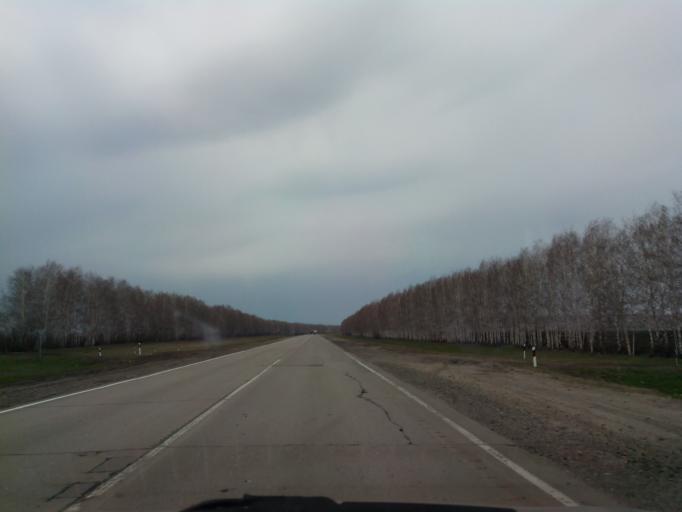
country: RU
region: Tambov
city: Znamenka
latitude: 52.2708
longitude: 41.4915
